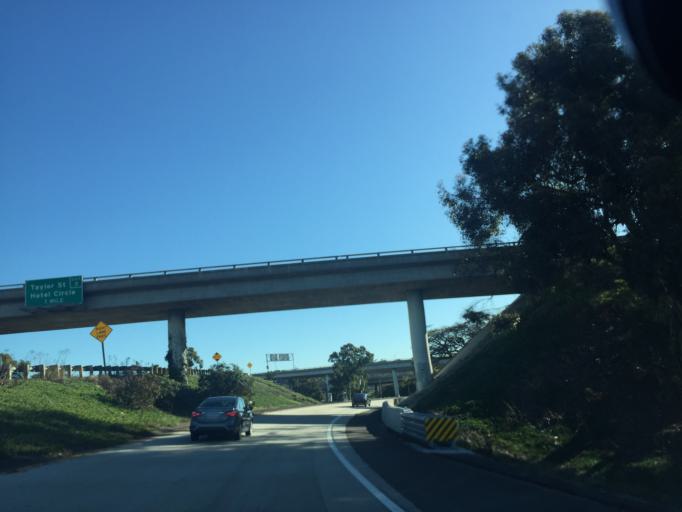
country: US
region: California
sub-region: San Diego County
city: San Diego
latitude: 32.7590
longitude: -117.2063
